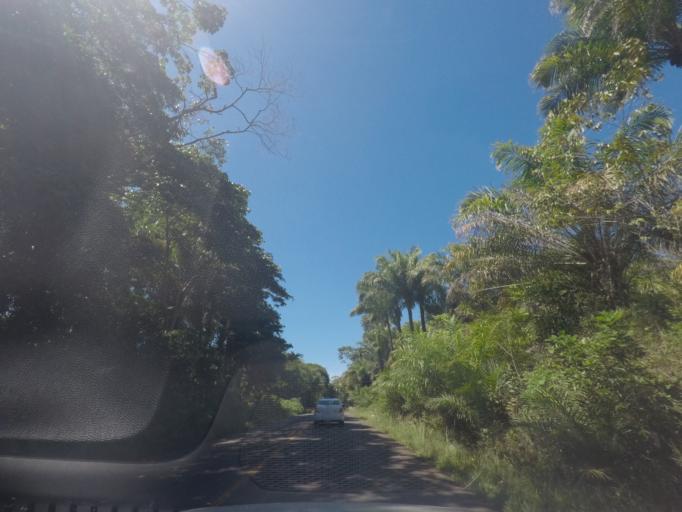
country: BR
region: Bahia
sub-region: Taperoa
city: Taperoa
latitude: -13.4623
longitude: -39.0889
